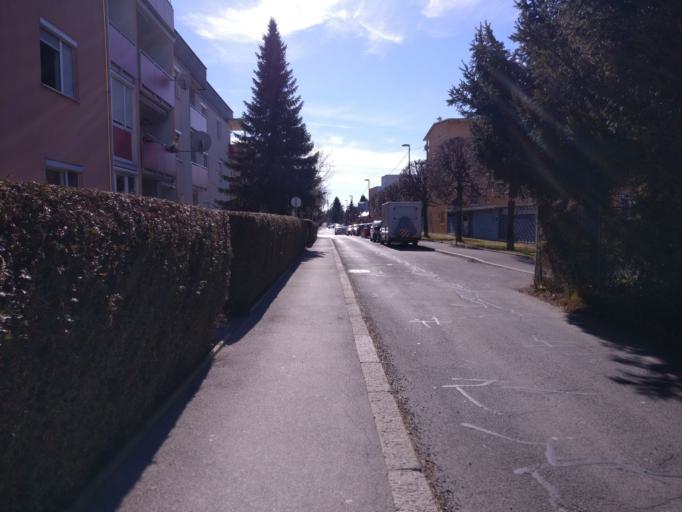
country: AT
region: Styria
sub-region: Graz Stadt
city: Wetzelsdorf
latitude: 47.0584
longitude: 15.4008
